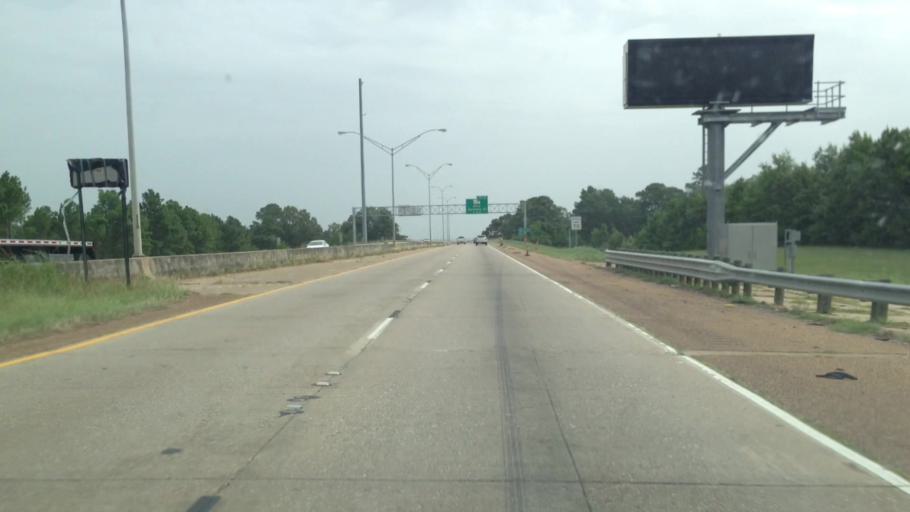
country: US
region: Louisiana
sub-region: Caddo Parish
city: Shreveport
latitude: 32.4929
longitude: -93.8228
